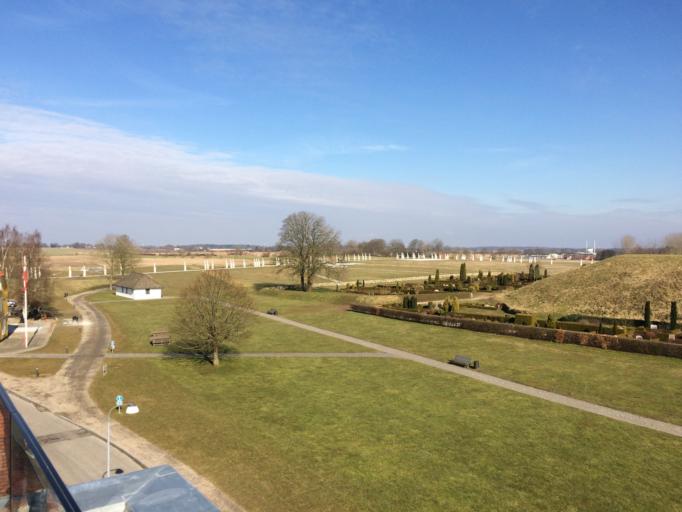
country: DK
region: South Denmark
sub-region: Vejle Kommune
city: Jelling
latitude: 55.7570
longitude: 9.4184
